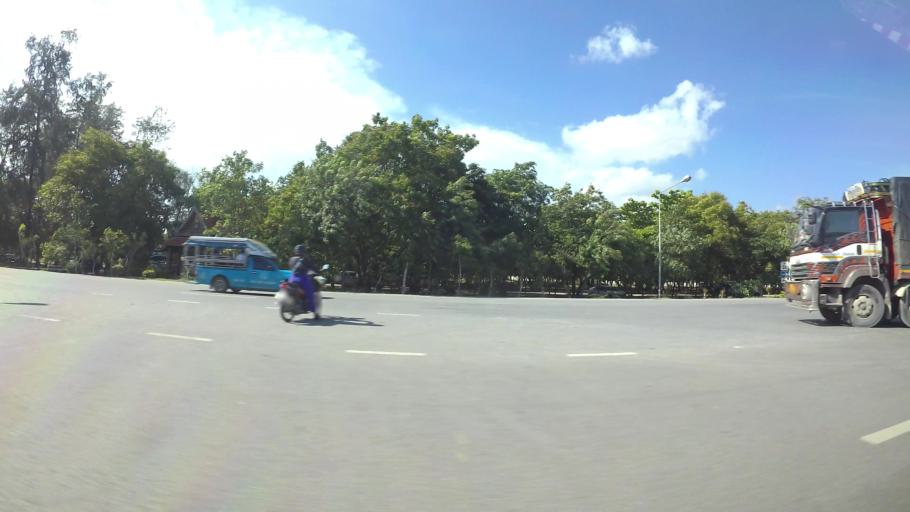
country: TH
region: Rayong
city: Rayong
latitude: 12.6630
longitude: 101.3080
